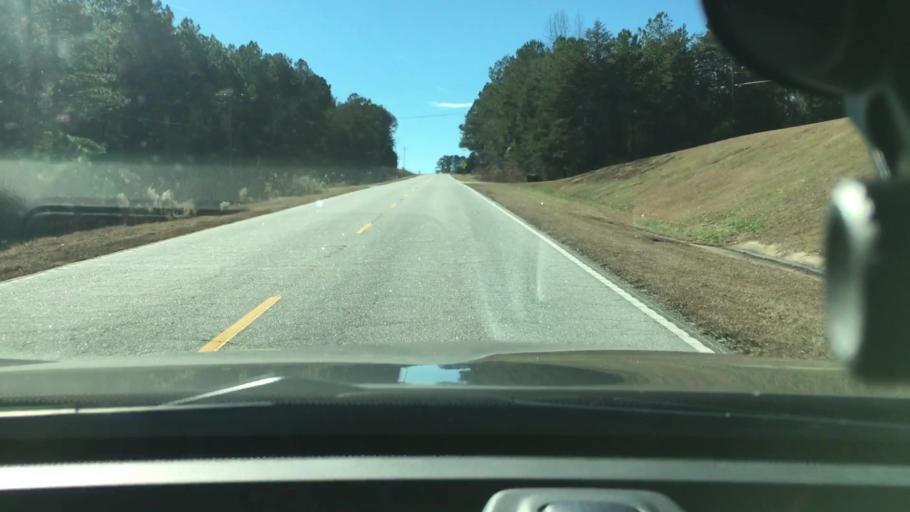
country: US
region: South Carolina
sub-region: Spartanburg County
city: Pacolet
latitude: 34.9569
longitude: -81.7115
